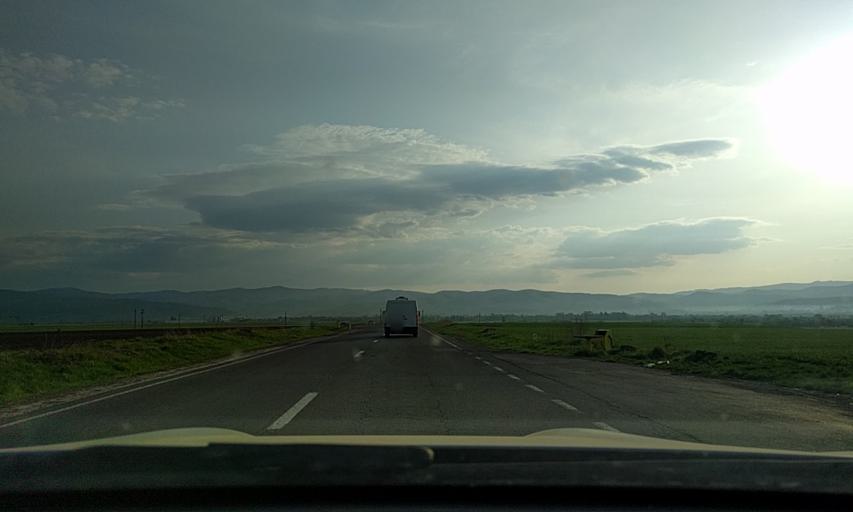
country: RO
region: Covasna
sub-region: Comuna Lemnia
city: Lemnia
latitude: 46.0355
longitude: 26.2417
